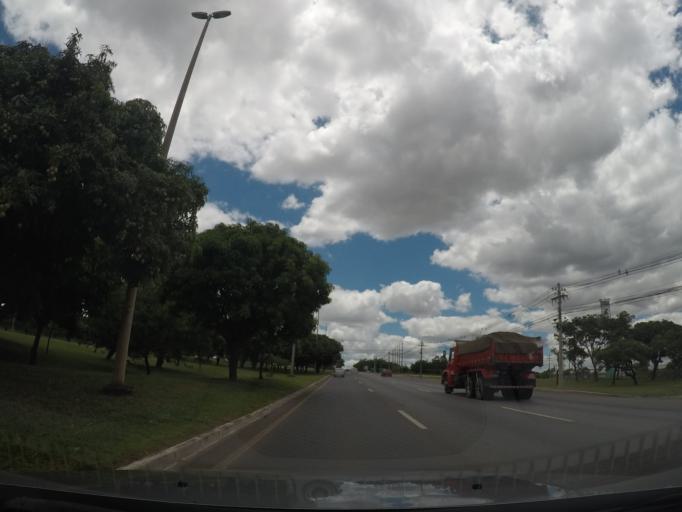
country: BR
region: Federal District
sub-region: Brasilia
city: Brasilia
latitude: -15.7546
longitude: -47.9261
